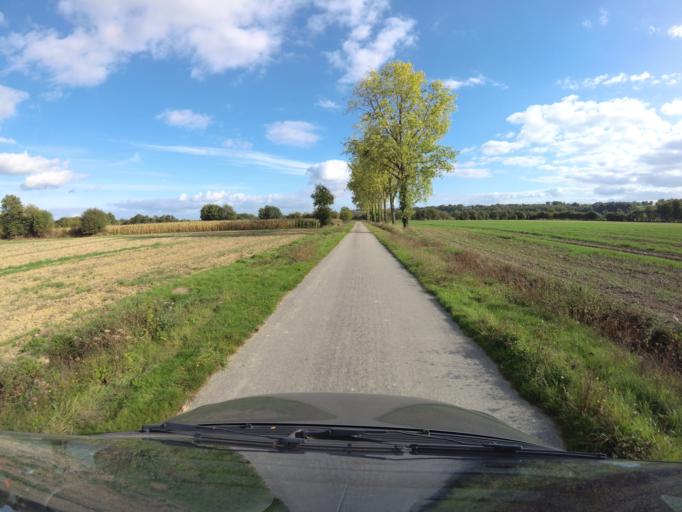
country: FR
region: Brittany
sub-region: Departement du Morbihan
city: Saint-Martin-sur-Oust
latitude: 47.7361
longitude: -2.2373
